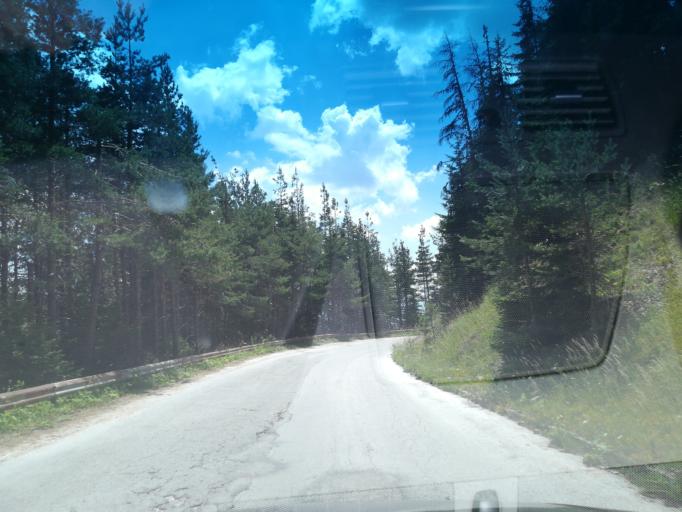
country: BG
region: Smolyan
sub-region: Obshtina Chepelare
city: Chepelare
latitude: 41.6881
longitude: 24.7578
